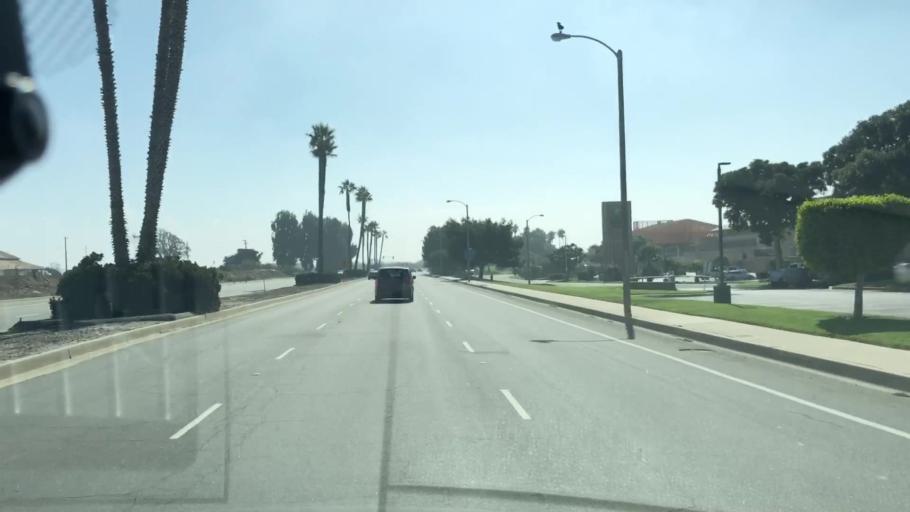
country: US
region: California
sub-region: Ventura County
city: Ventura
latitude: 34.2479
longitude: -119.2577
